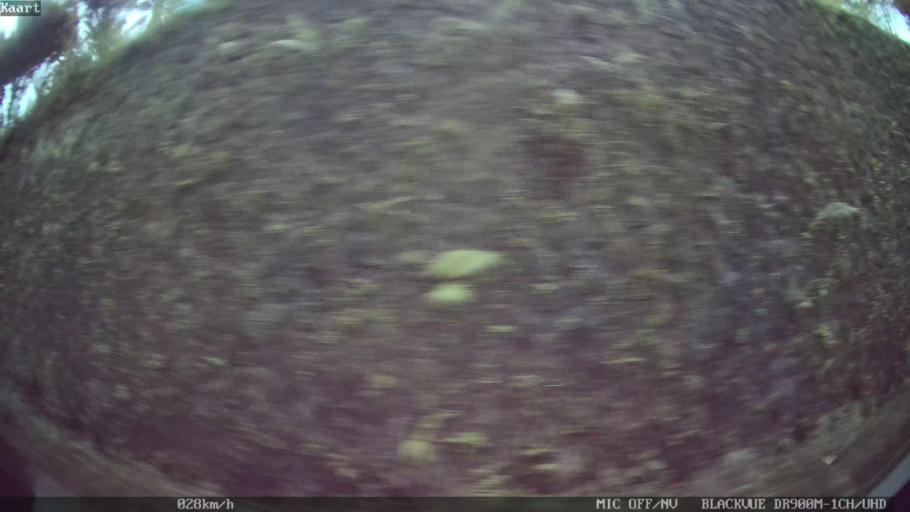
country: ID
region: Bali
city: Banjar Susut Kaja
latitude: -8.4438
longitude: 115.3379
